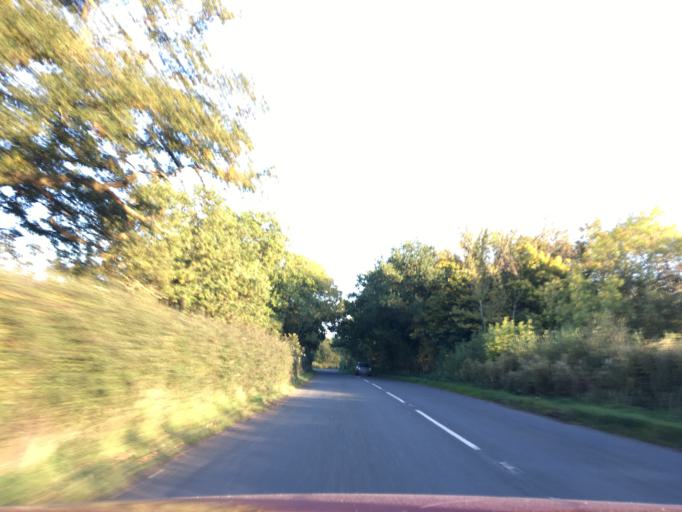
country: GB
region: England
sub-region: Worcestershire
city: Great Malvern
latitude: 52.0185
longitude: -2.3226
